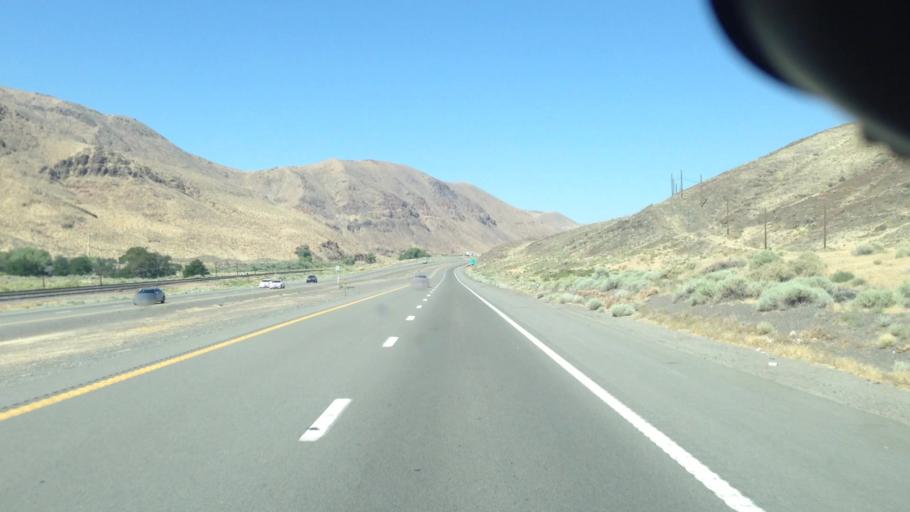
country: US
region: Nevada
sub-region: Lyon County
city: Fernley
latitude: 39.5910
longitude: -119.4177
